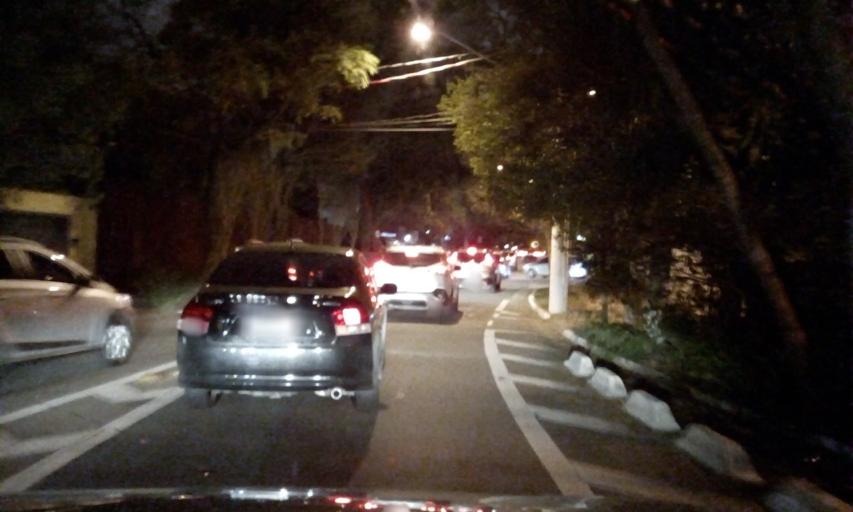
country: BR
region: Sao Paulo
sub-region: Sao Paulo
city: Sao Paulo
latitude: -23.5713
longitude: -46.6773
